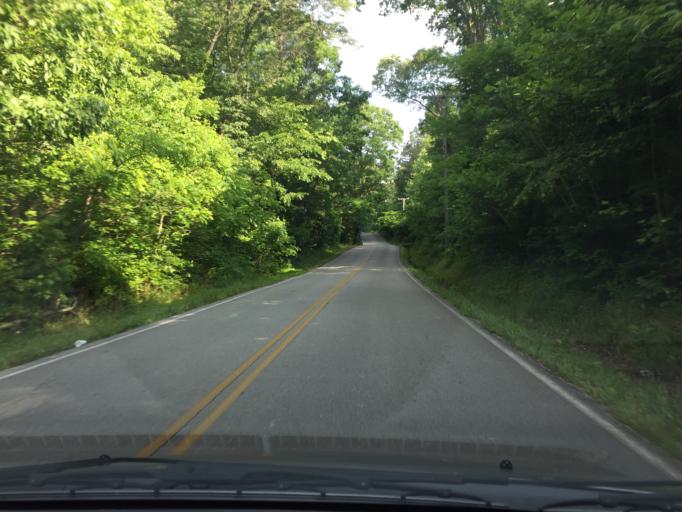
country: US
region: Tennessee
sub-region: Hamilton County
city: Collegedale
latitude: 35.0832
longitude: -85.0096
